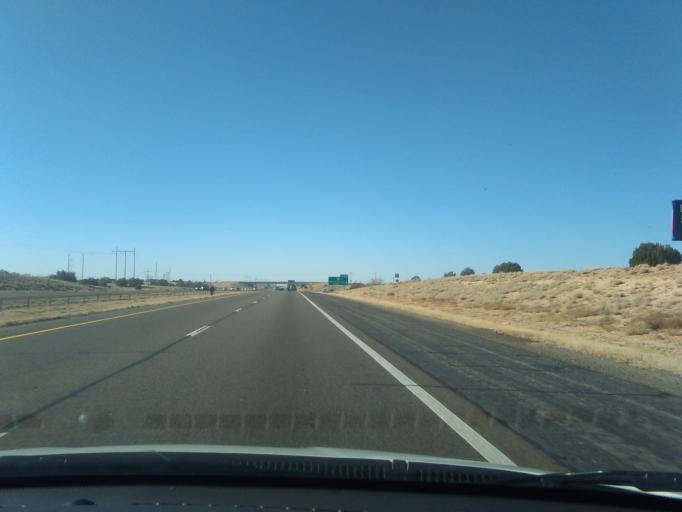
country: US
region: New Mexico
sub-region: Sandoval County
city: Santo Domingo Pueblo
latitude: 35.4737
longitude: -106.2967
